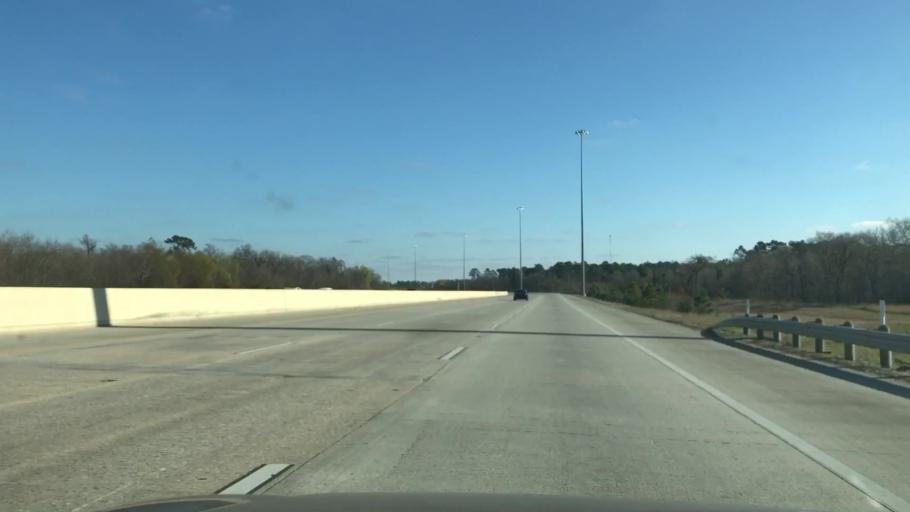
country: US
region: Texas
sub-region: Harris County
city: Jacinto City
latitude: 29.7936
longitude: -95.2311
